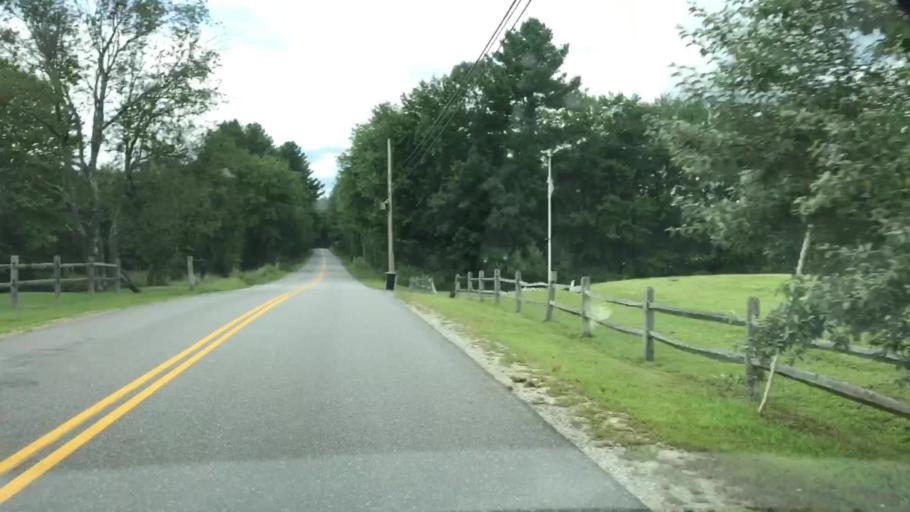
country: US
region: New Hampshire
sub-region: Hillsborough County
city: Milford
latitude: 42.8223
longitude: -71.5963
